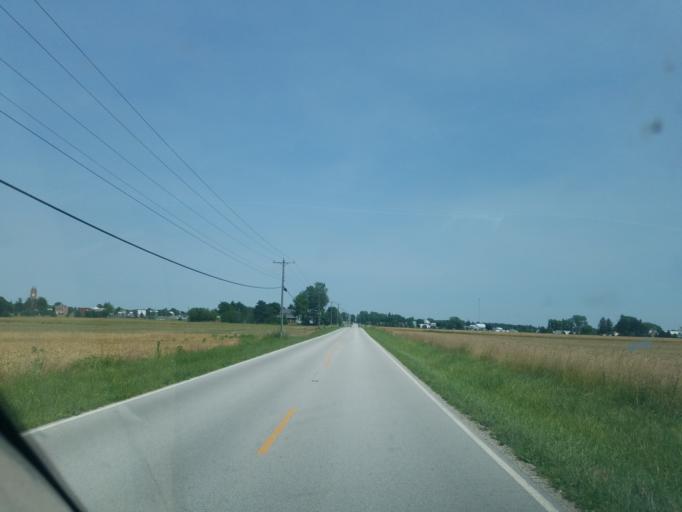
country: US
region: Ohio
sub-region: Wyandot County
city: Carey
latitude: 41.0507
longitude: -83.3291
